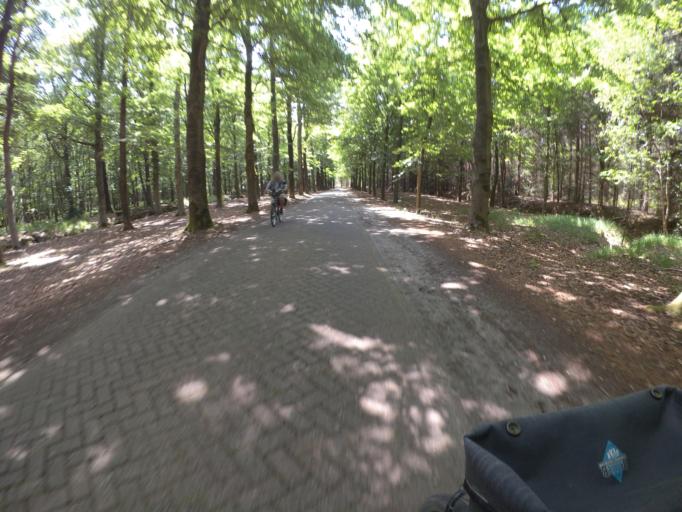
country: NL
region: North Brabant
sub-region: Gemeente Oirschot
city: Oostelbeers
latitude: 51.4863
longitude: 5.2555
